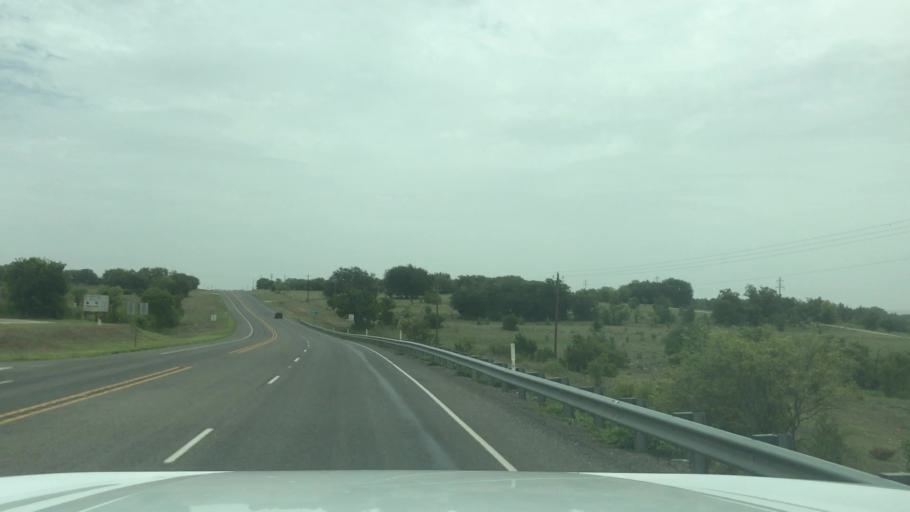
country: US
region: Texas
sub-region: Hamilton County
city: Hico
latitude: 31.9807
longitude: -98.0218
